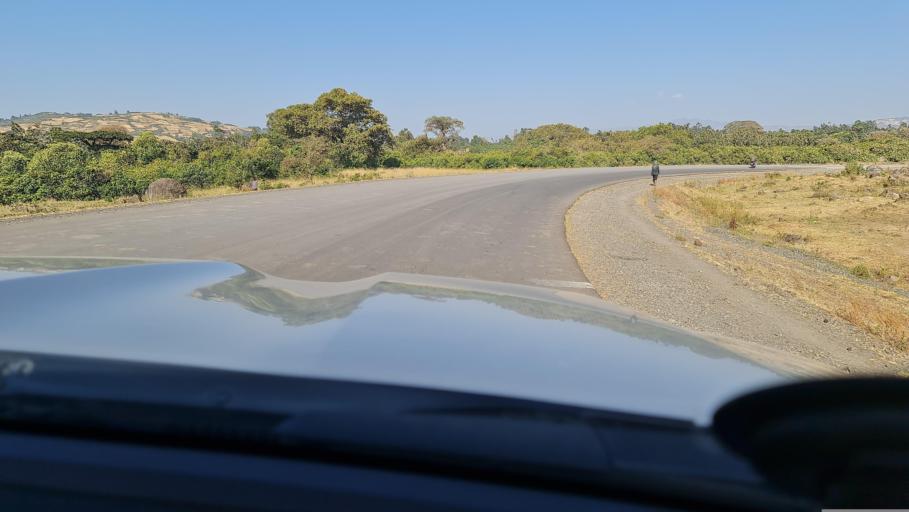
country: ET
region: Oromiya
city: Waliso
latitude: 8.5649
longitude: 37.9450
